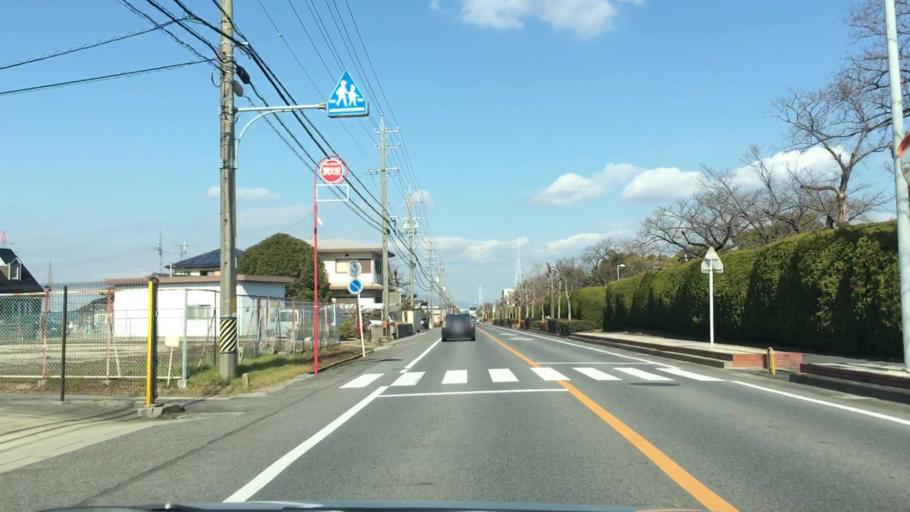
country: JP
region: Aichi
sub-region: Toyota-shi
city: Toyota
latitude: 35.0210
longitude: 137.1266
